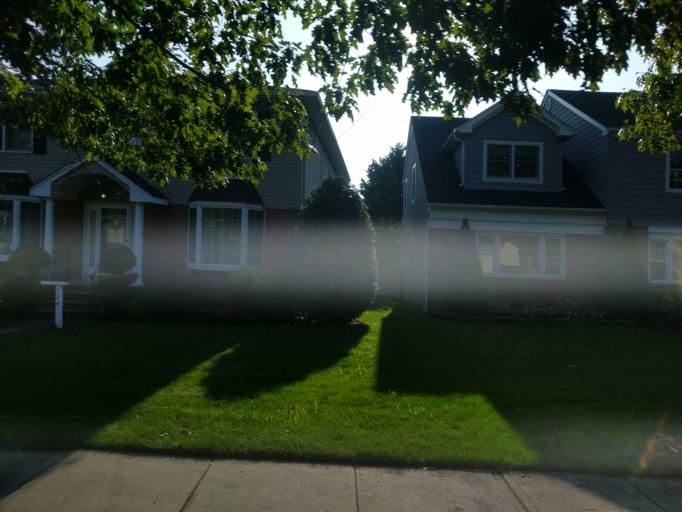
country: US
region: New York
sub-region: Nassau County
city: Malverne
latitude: 40.6702
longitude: -73.6704
